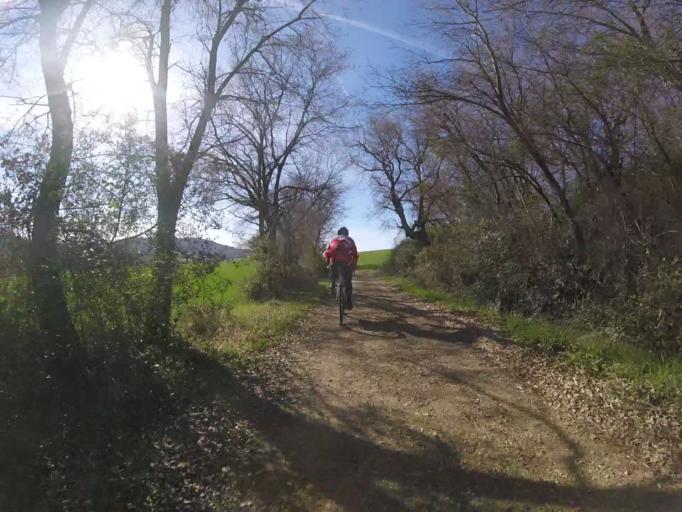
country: ES
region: Navarre
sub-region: Provincia de Navarra
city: Villatuerta
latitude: 42.6717
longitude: -1.9594
